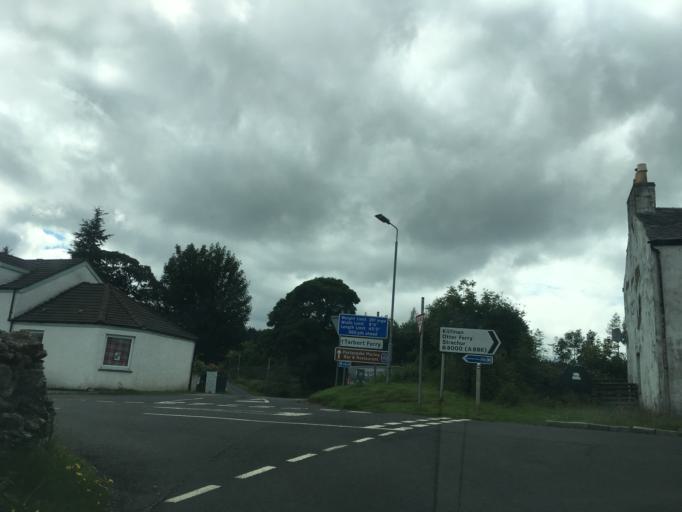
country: GB
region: Scotland
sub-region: Argyll and Bute
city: Tarbert
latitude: 55.8847
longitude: -5.2693
